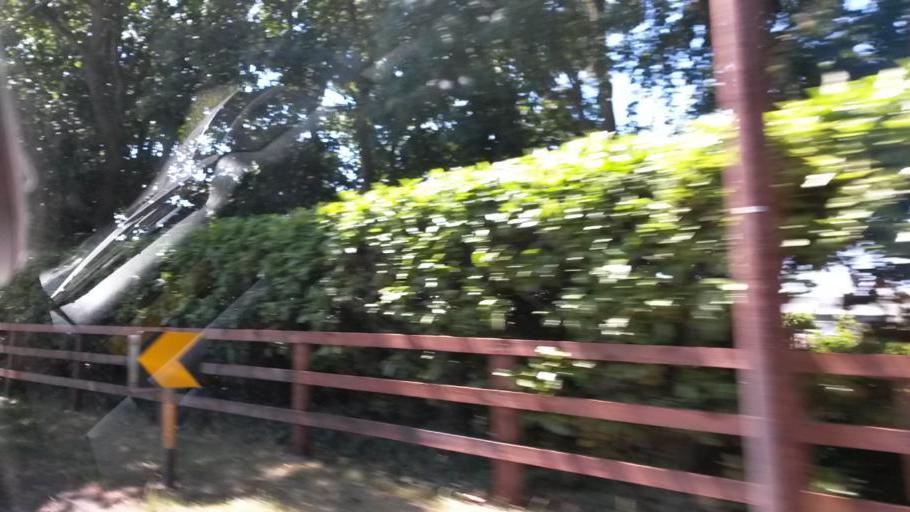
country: IE
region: Leinster
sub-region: Fingal County
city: Swords
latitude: 53.4628
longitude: -6.2722
